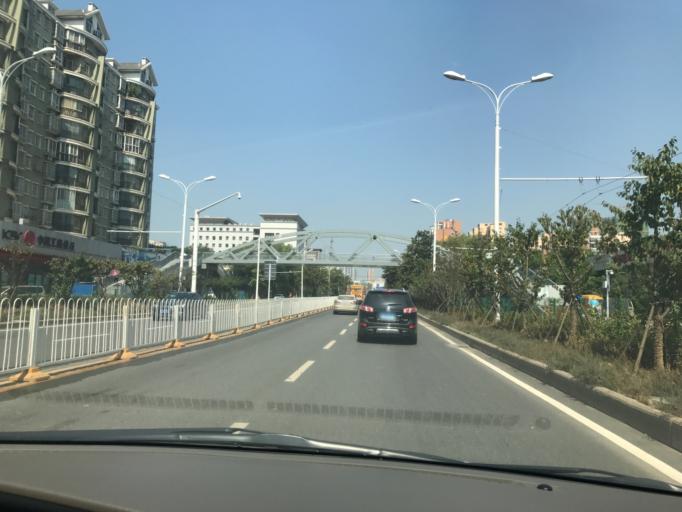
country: CN
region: Hubei
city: Yongfeng
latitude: 30.5605
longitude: 114.2192
